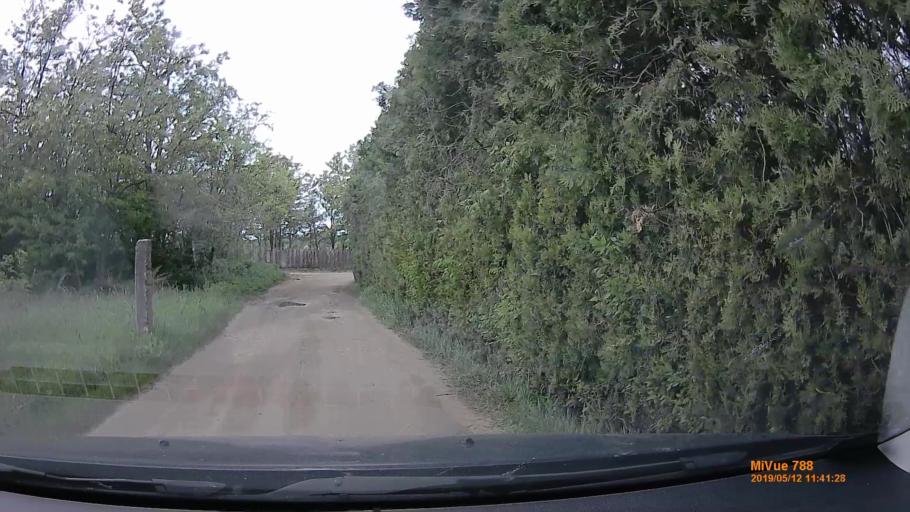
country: HU
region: Budapest
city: Budapest XVII. keruelet
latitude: 47.4621
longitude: 19.2560
